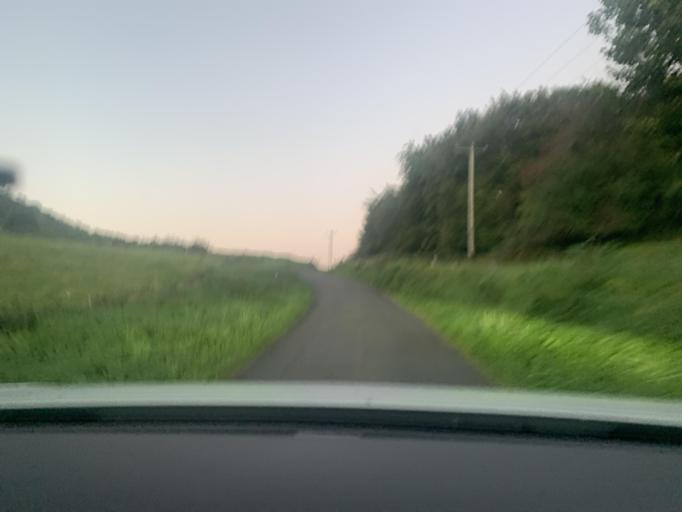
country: IE
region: Connaught
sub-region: County Leitrim
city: Manorhamilton
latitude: 54.2610
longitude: -8.2960
